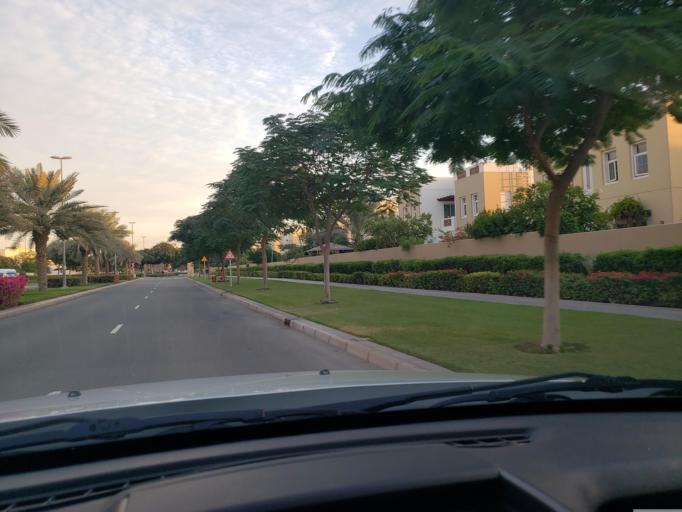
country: AE
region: Dubai
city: Dubai
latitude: 25.0258
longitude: 55.2683
